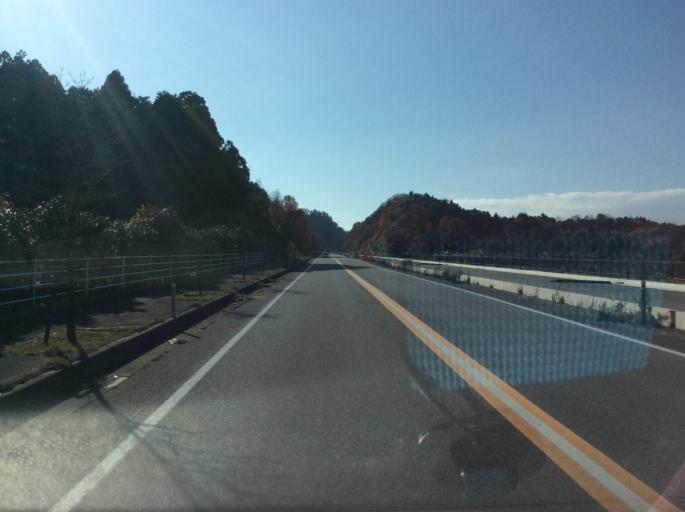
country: JP
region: Fukushima
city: Iwaki
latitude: 37.0482
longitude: 140.9405
